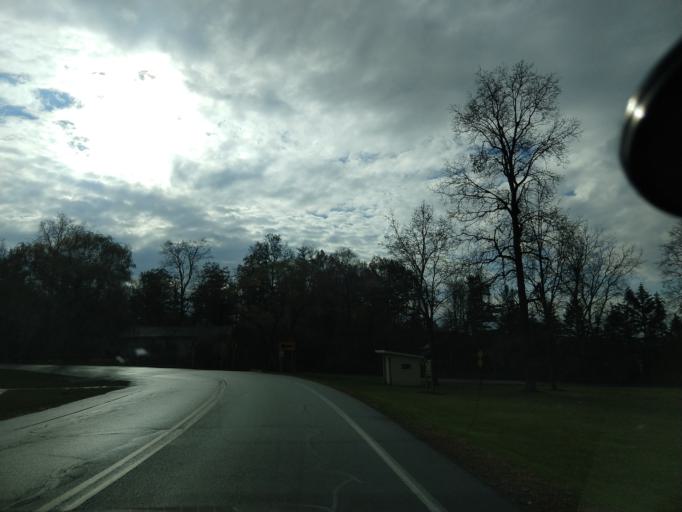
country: US
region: New York
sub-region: Tompkins County
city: Lansing
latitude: 42.4788
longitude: -76.4728
